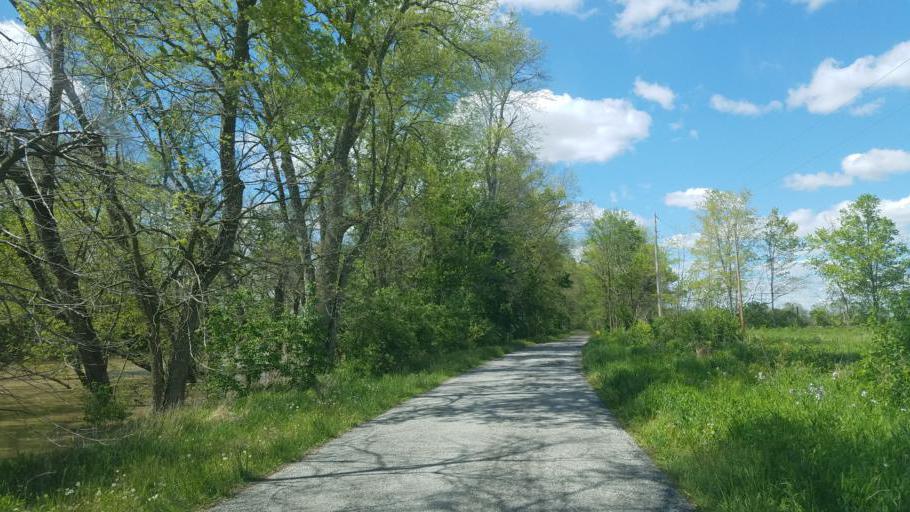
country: US
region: Ohio
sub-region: Marion County
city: Prospect
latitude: 40.4282
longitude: -83.1921
